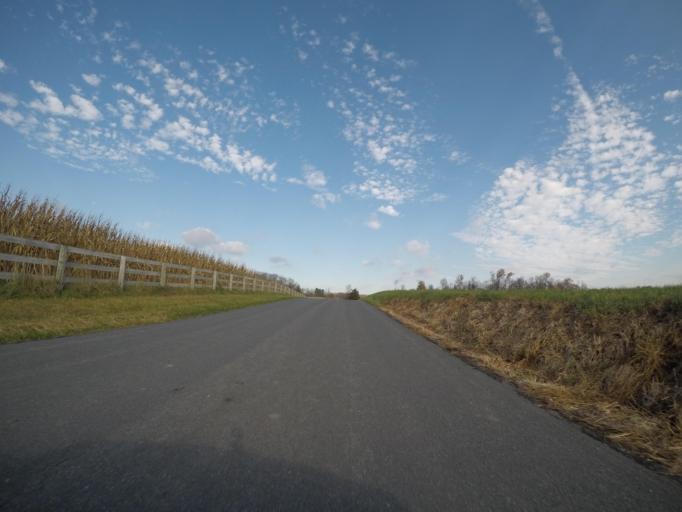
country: US
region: Maryland
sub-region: Carroll County
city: Hampstead
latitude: 39.5578
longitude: -76.8140
